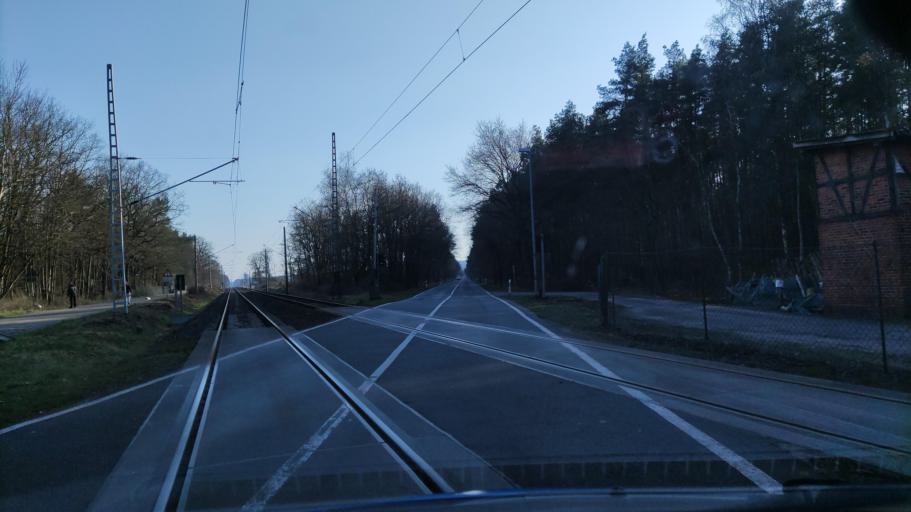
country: DE
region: Saxony-Anhalt
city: Seehausen
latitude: 52.8738
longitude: 11.7421
